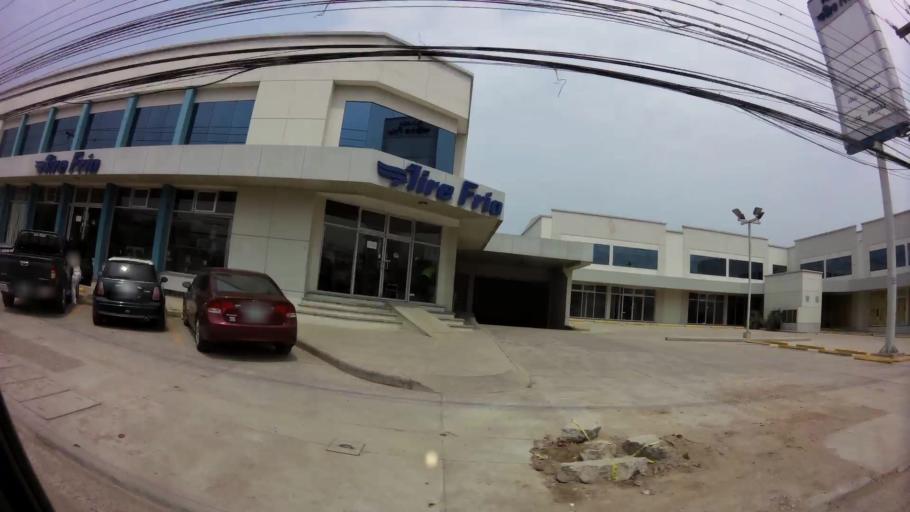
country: HN
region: Francisco Morazan
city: Tegucigalpa
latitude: 14.0866
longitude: -87.2089
